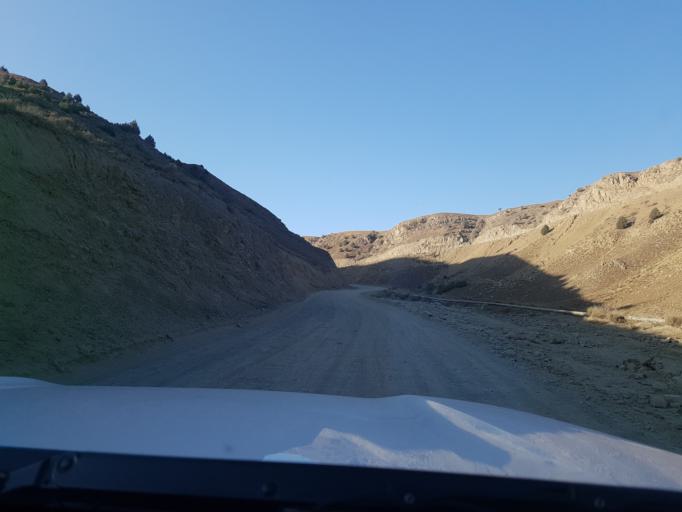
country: TM
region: Ahal
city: Baharly
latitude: 38.4456
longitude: 57.0492
